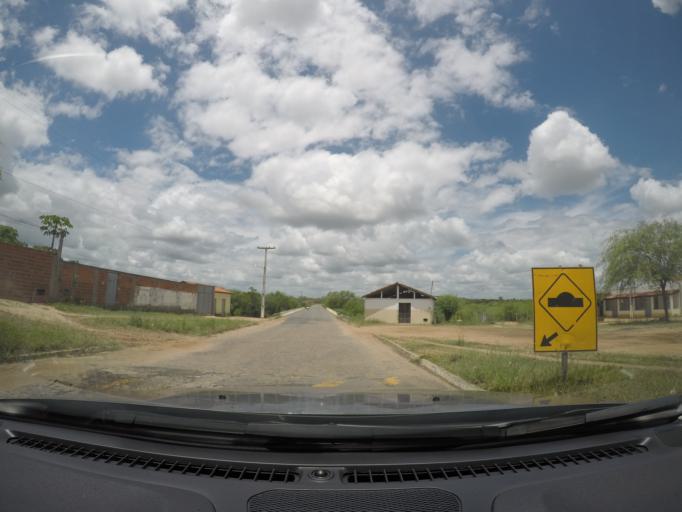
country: BR
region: Bahia
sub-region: Itaberaba
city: Itaberaba
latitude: -12.3611
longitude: -40.0388
